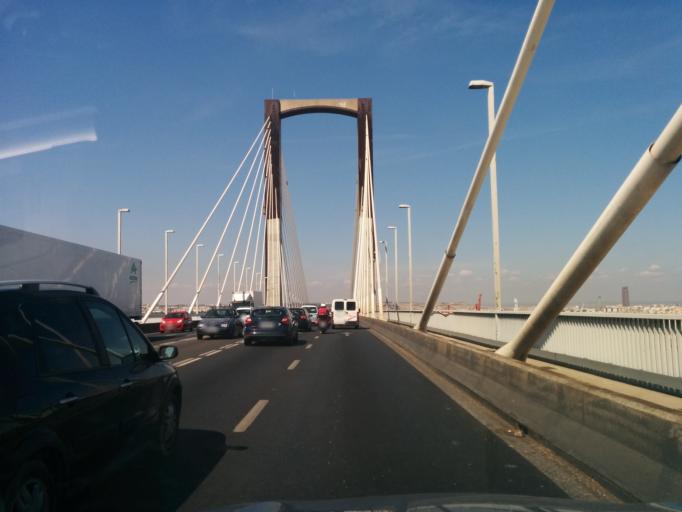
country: ES
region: Andalusia
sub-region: Provincia de Sevilla
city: Gelves
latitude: 37.3489
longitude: -5.9929
